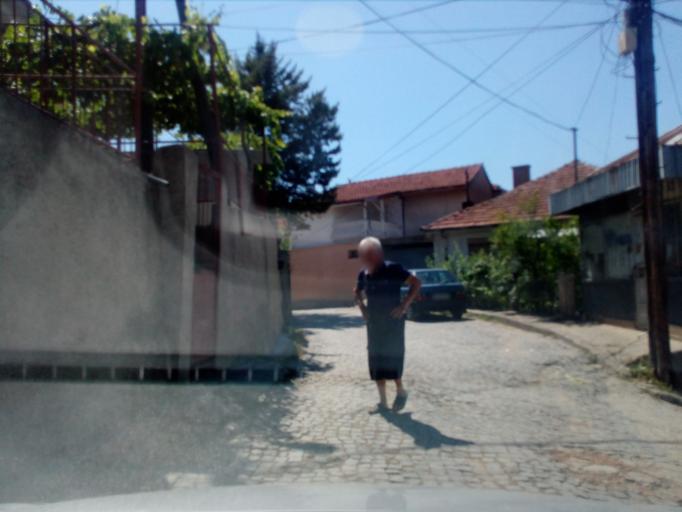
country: MK
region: Veles
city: Veles
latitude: 41.7209
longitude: 21.7891
